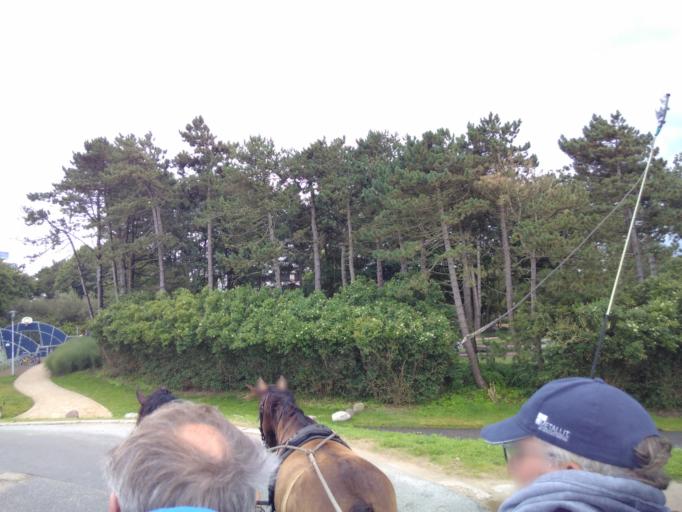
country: DE
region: Lower Saxony
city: Cuxhaven
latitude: 53.8874
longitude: 8.6477
